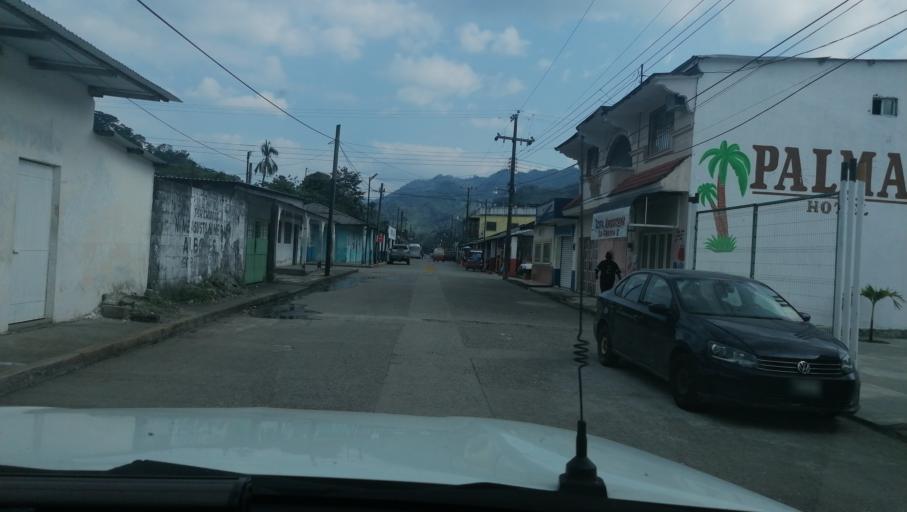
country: MX
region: Chiapas
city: Ostuacan
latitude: 17.4084
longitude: -93.3370
